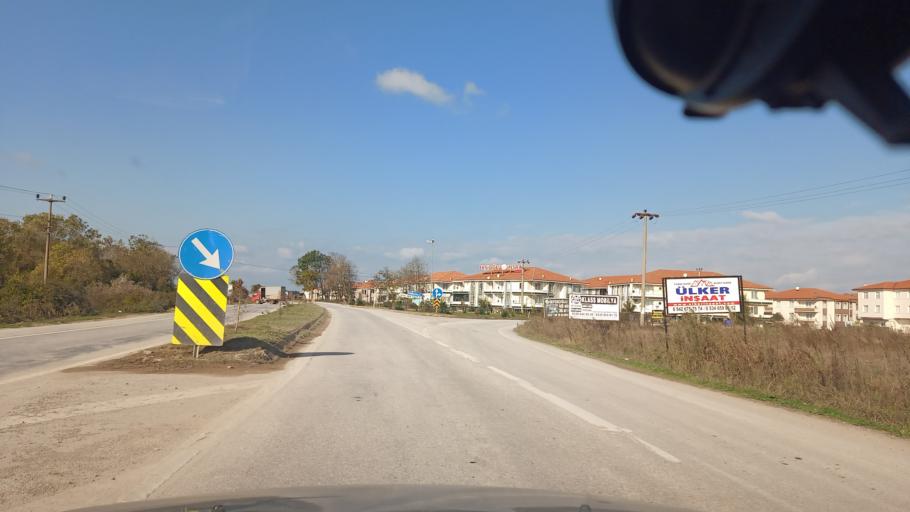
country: TR
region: Sakarya
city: Karasu
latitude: 41.1166
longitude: 30.6521
